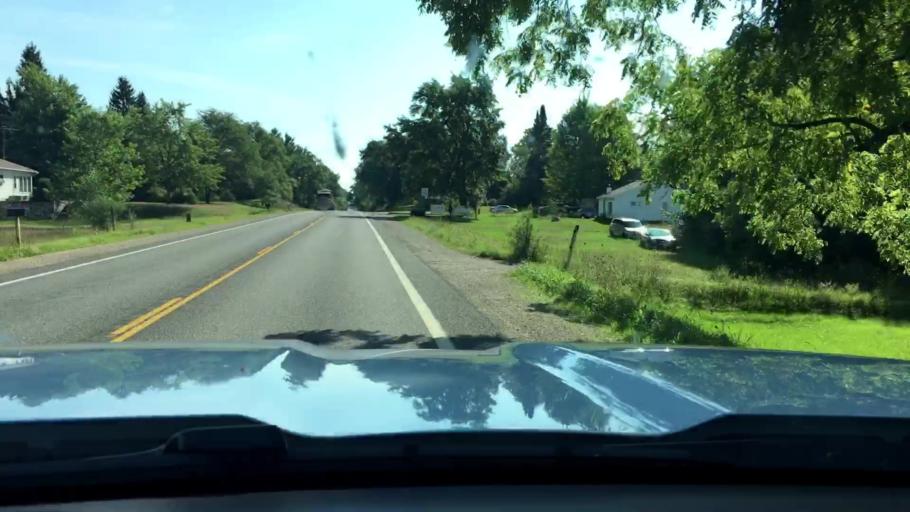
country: US
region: Michigan
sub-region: Montcalm County
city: Edmore
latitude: 43.4083
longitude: -84.8623
